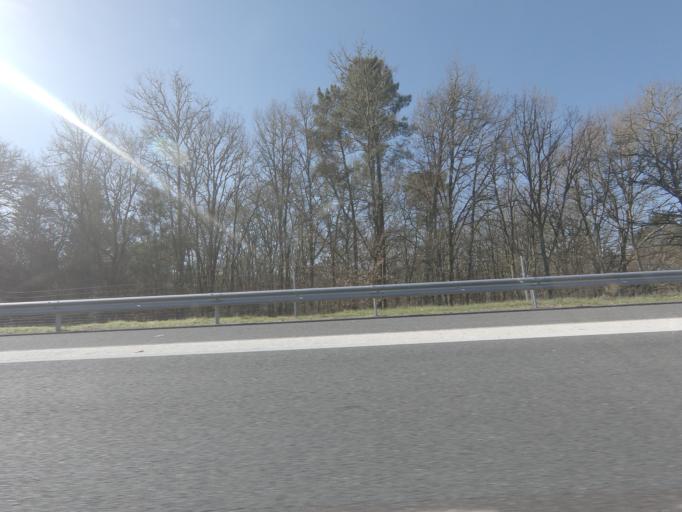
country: ES
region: Galicia
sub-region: Provincia de Ourense
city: Maside
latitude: 42.4024
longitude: -8.0083
